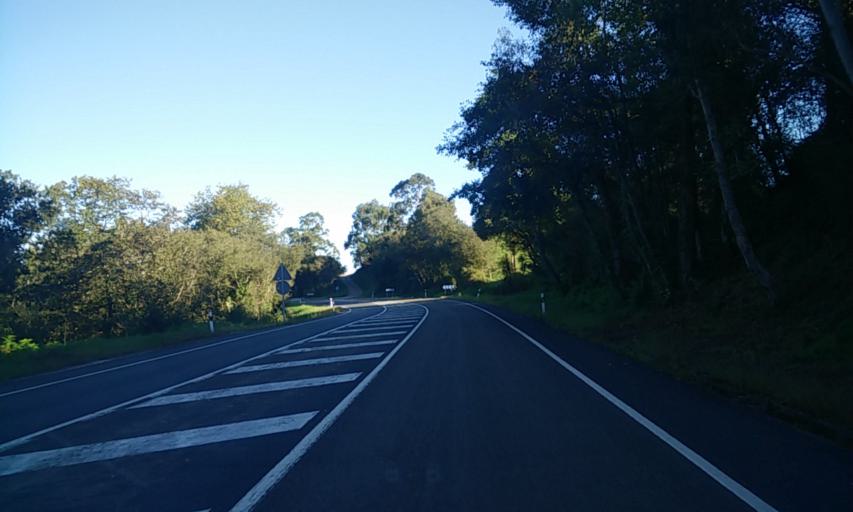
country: ES
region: Cantabria
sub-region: Provincia de Cantabria
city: San Vicente de la Barquera
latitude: 43.3759
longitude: -4.3731
